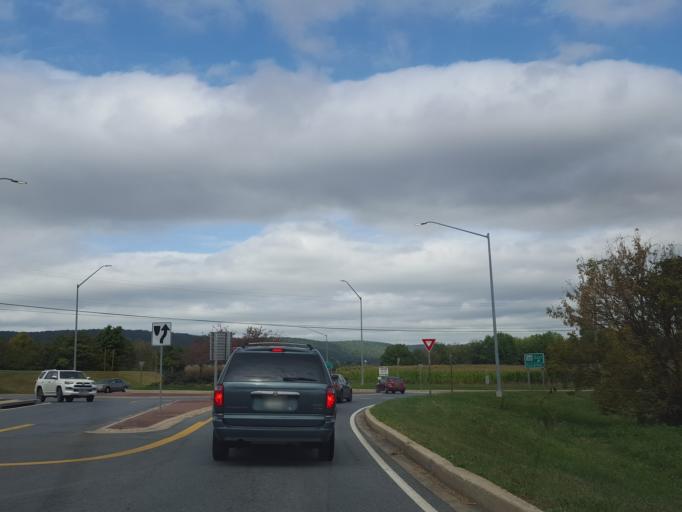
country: US
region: Maryland
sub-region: Frederick County
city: Brunswick
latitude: 39.3372
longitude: -77.6392
